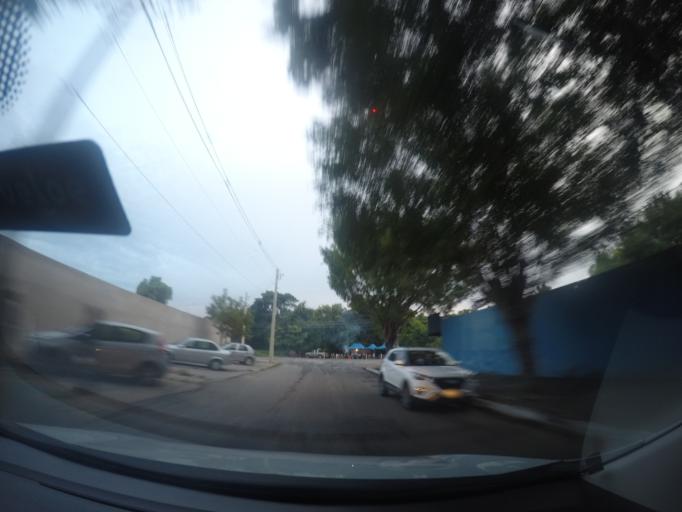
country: BR
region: Goias
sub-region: Goiania
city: Goiania
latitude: -16.6448
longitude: -49.2444
